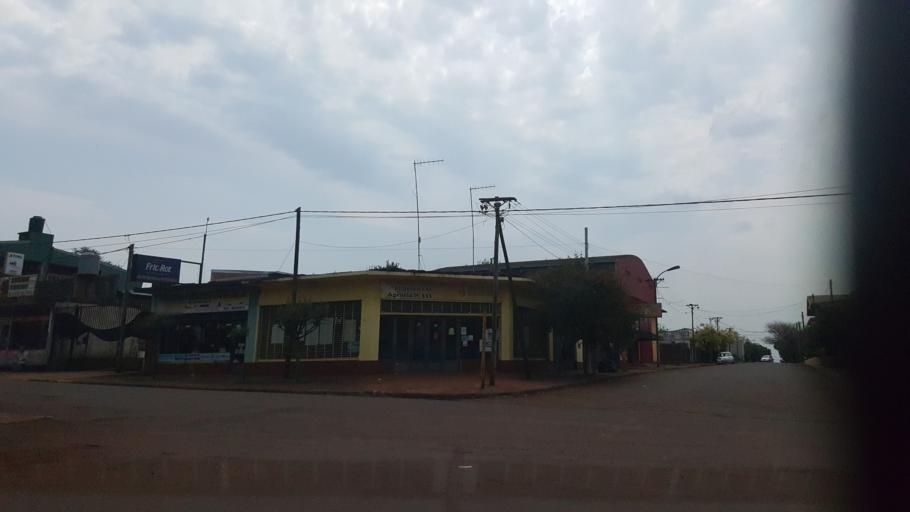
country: AR
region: Misiones
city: Jardin America
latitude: -27.0457
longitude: -55.2401
